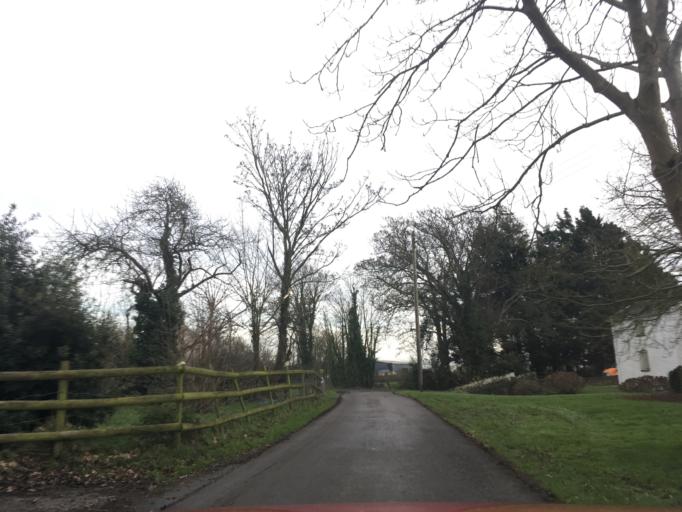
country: GB
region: Wales
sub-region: Newport
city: Redwick
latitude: 51.5527
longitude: -2.8509
